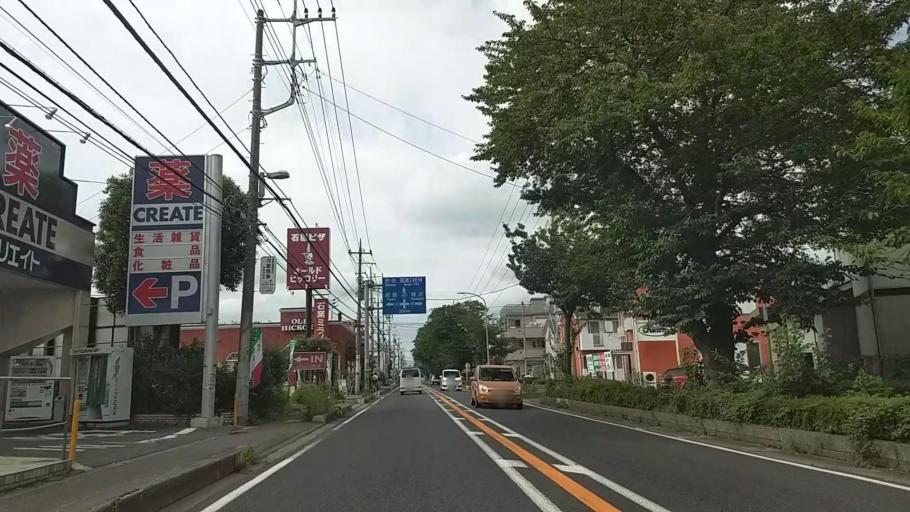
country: JP
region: Kanagawa
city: Minami-rinkan
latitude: 35.4460
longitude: 139.4674
